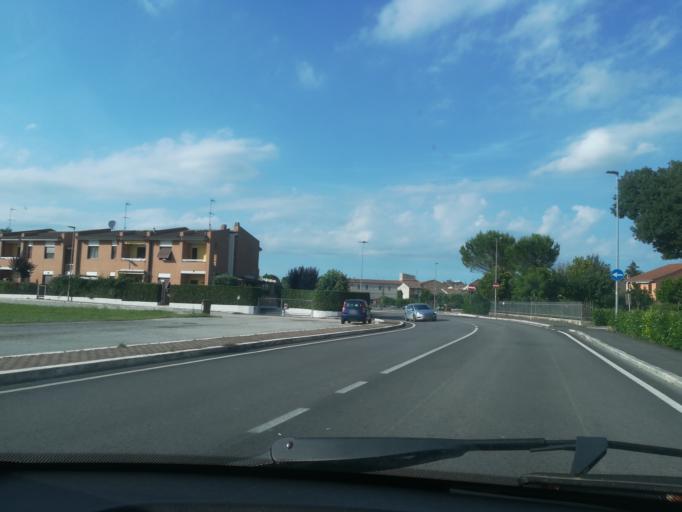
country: IT
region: The Marches
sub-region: Provincia di Macerata
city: Villa Potenza
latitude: 43.3206
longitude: 13.4244
